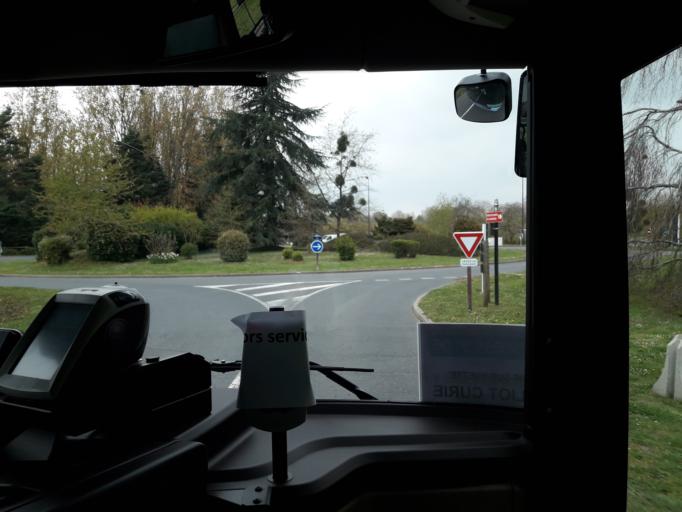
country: FR
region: Ile-de-France
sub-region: Departement de l'Essonne
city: Vauhallan
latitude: 48.7163
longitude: 2.2185
